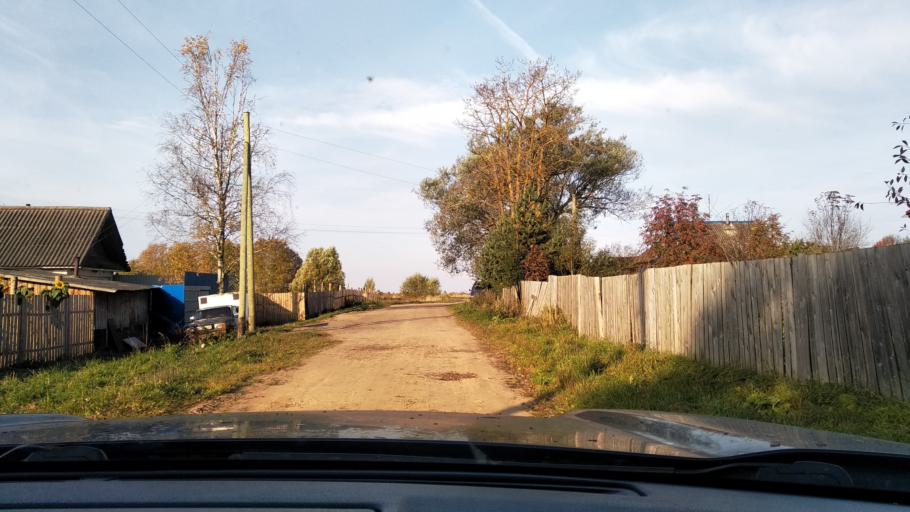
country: RU
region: Tverskaya
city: Krasnyy Kholm
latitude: 58.0094
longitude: 37.1856
